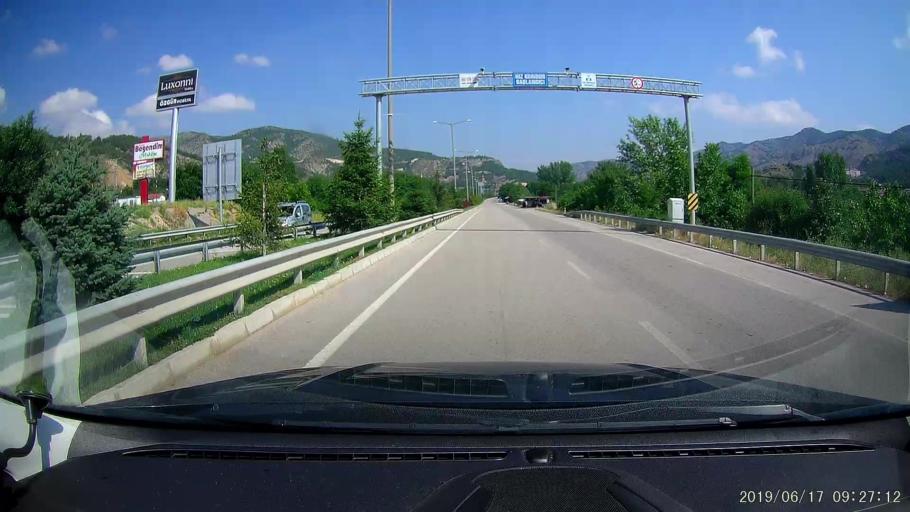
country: TR
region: Amasya
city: Amasya
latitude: 40.6748
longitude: 35.8283
